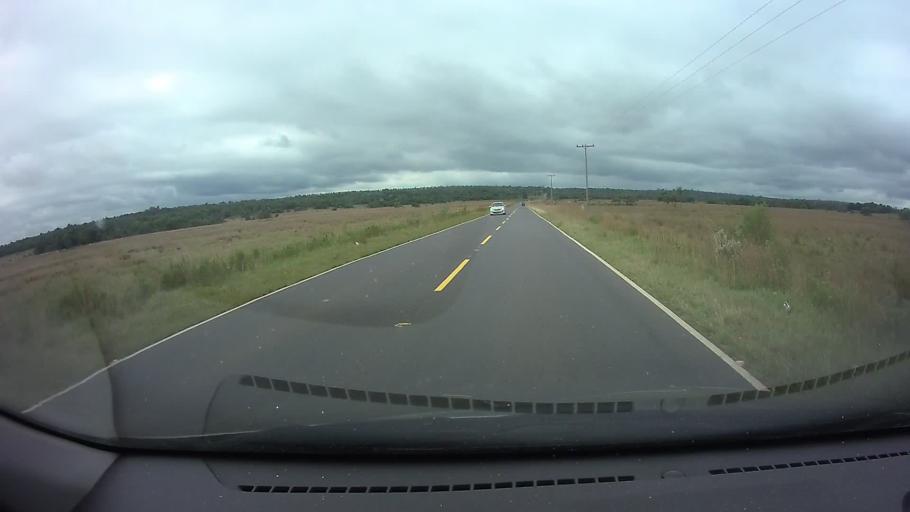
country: PY
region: Paraguari
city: Yaguaron
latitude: -25.7105
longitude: -57.3453
